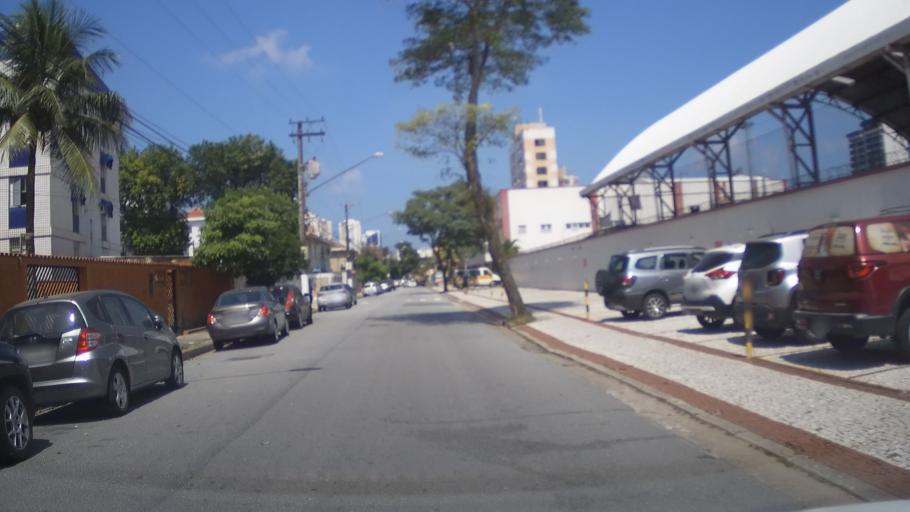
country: BR
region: Sao Paulo
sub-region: Santos
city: Santos
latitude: -23.9762
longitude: -46.3044
